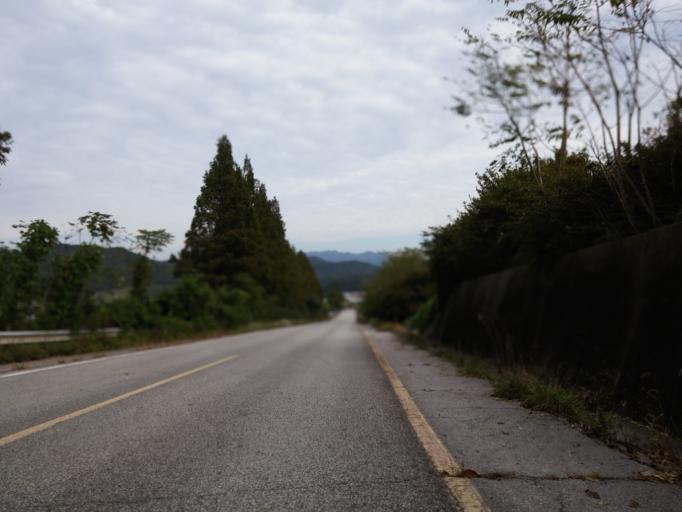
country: KR
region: Chungcheongnam-do
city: Yonmu
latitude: 36.1635
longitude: 127.1959
